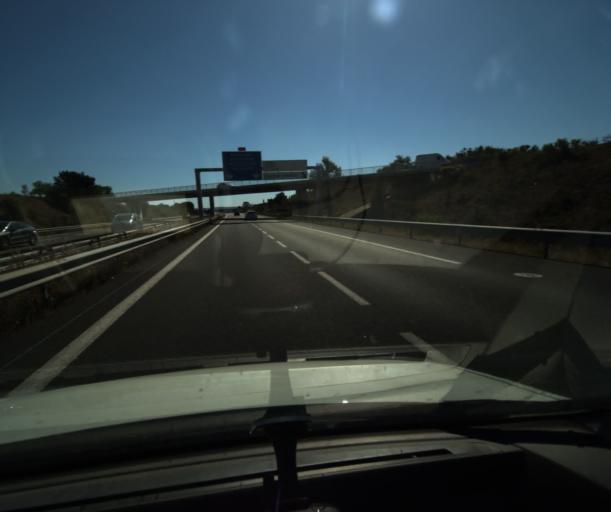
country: FR
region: Languedoc-Roussillon
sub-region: Departement de l'Aude
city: Ferrals-les-Corbieres
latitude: 43.1680
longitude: 2.7346
